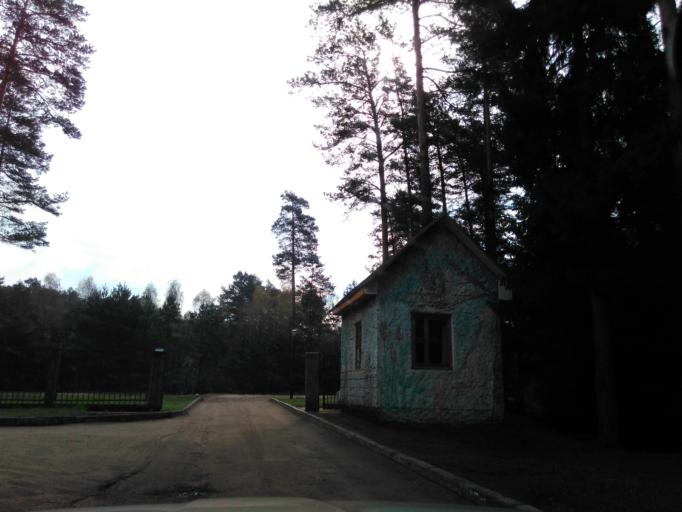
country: BY
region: Minsk
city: Rakaw
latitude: 53.9696
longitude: 27.0173
